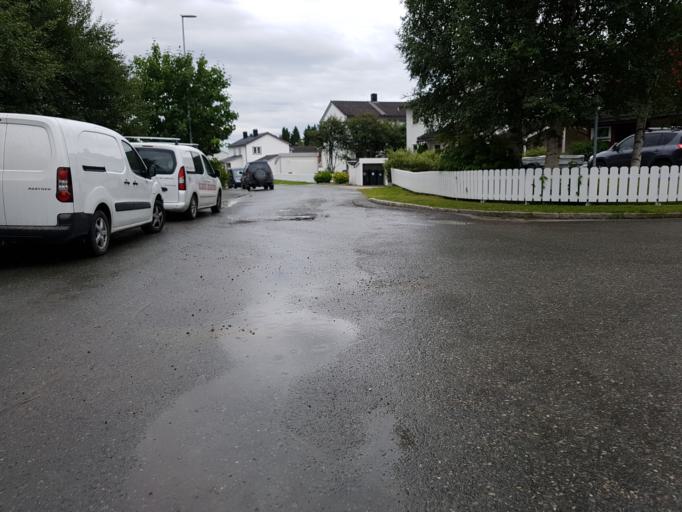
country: NO
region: Sor-Trondelag
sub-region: Trondheim
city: Trondheim
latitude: 63.3898
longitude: 10.3310
